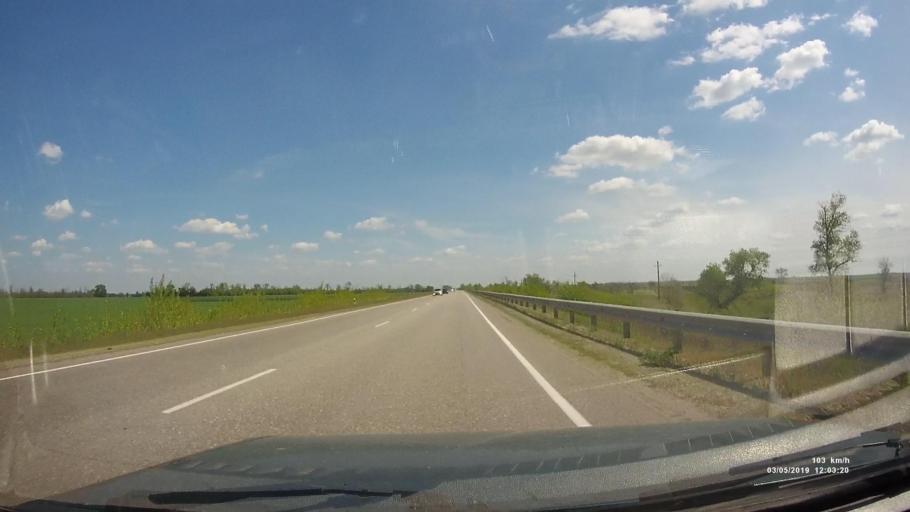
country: RU
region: Rostov
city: Bagayevskaya
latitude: 47.2737
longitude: 40.3877
